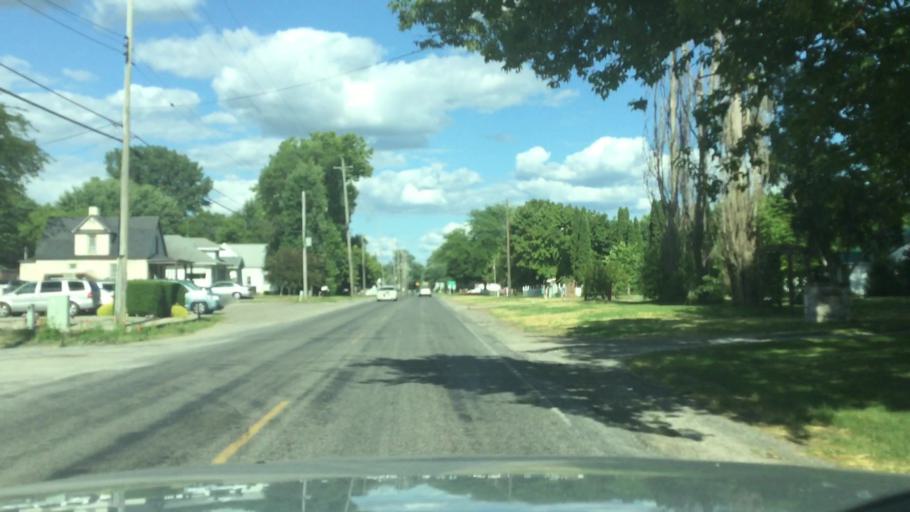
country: US
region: Michigan
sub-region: Saginaw County
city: Saginaw
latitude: 43.4008
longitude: -83.9977
